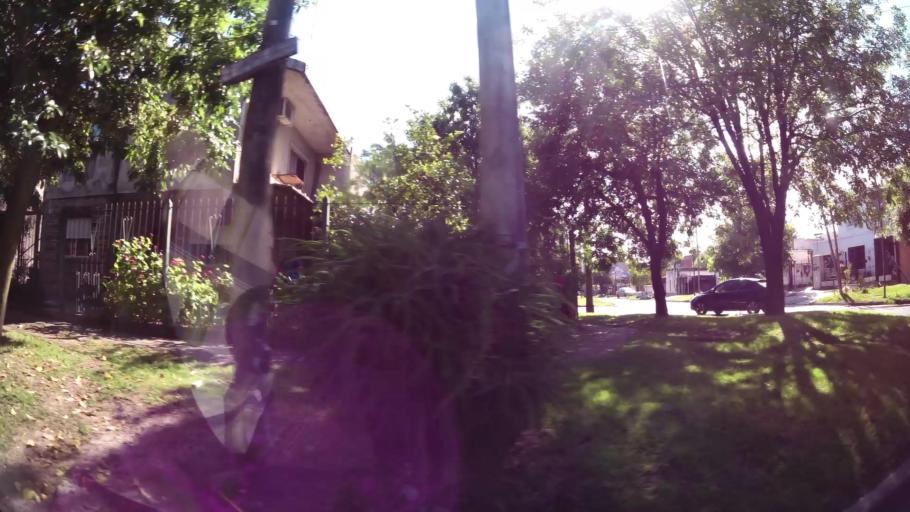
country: AR
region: Buenos Aires
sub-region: Partido de Tigre
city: Tigre
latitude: -34.4756
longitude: -58.5795
